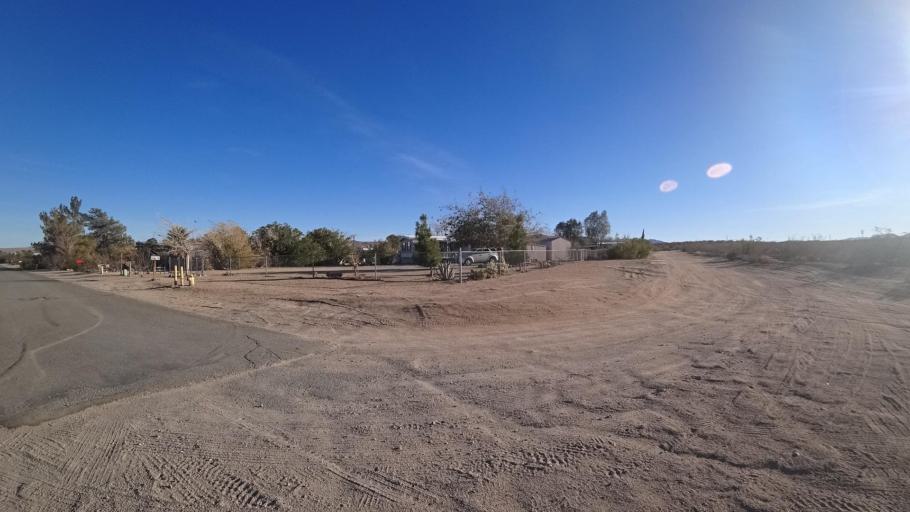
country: US
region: California
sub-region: Kern County
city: Ridgecrest
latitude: 35.6007
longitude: -117.7124
